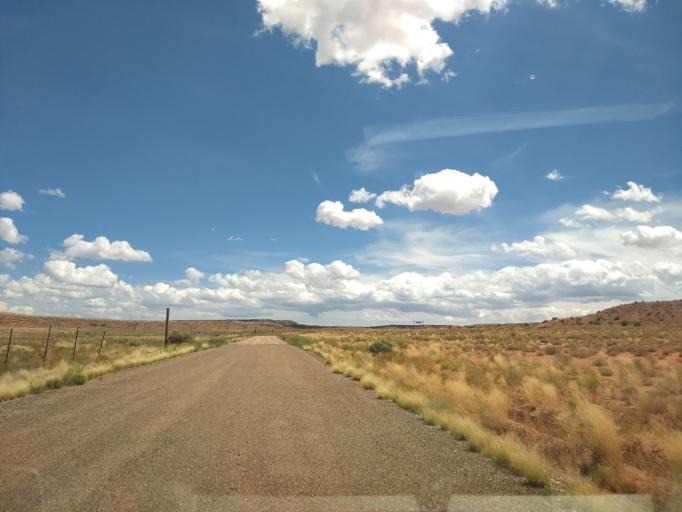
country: US
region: Arizona
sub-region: Coconino County
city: Fredonia
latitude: 36.9450
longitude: -112.5037
